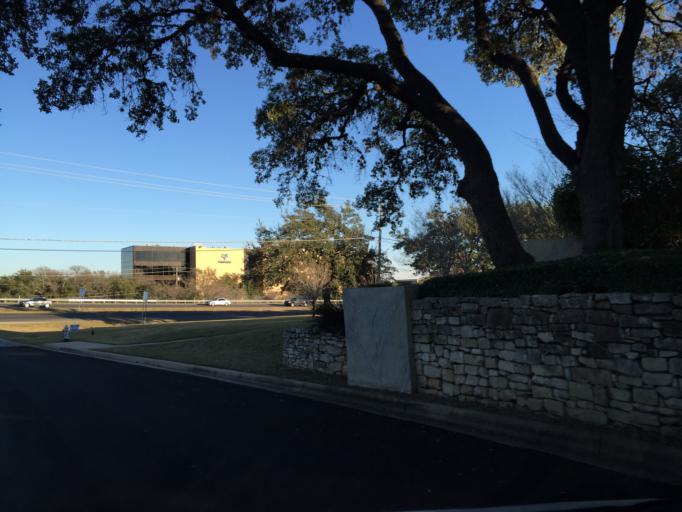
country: US
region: Texas
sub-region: Travis County
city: Rollingwood
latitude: 30.2739
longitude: -97.8185
